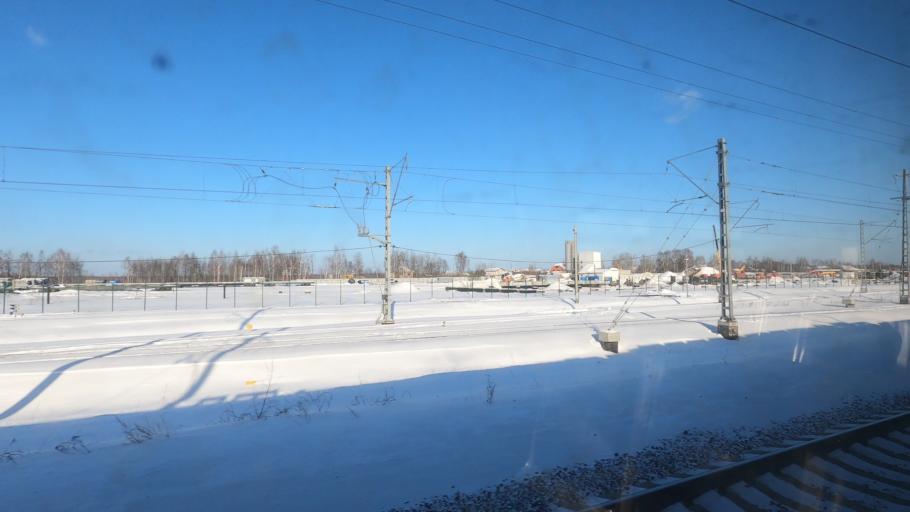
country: RU
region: Moskovskaya
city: Elektrougli
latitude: 55.7231
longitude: 38.2493
